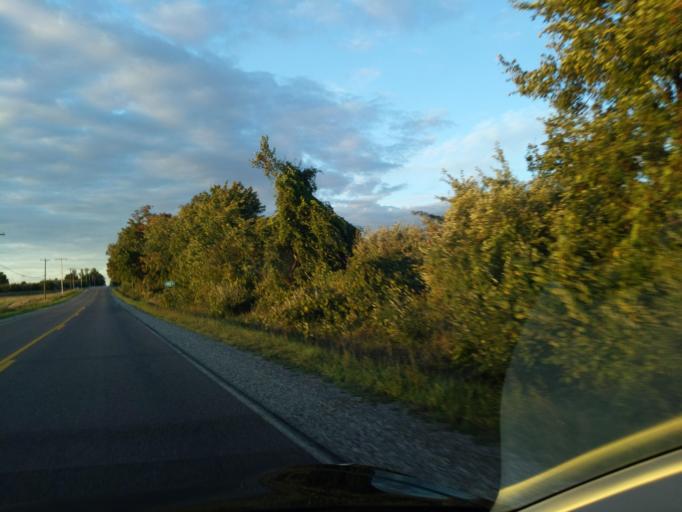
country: US
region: Michigan
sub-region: Antrim County
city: Elk Rapids
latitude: 44.8286
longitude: -85.4051
